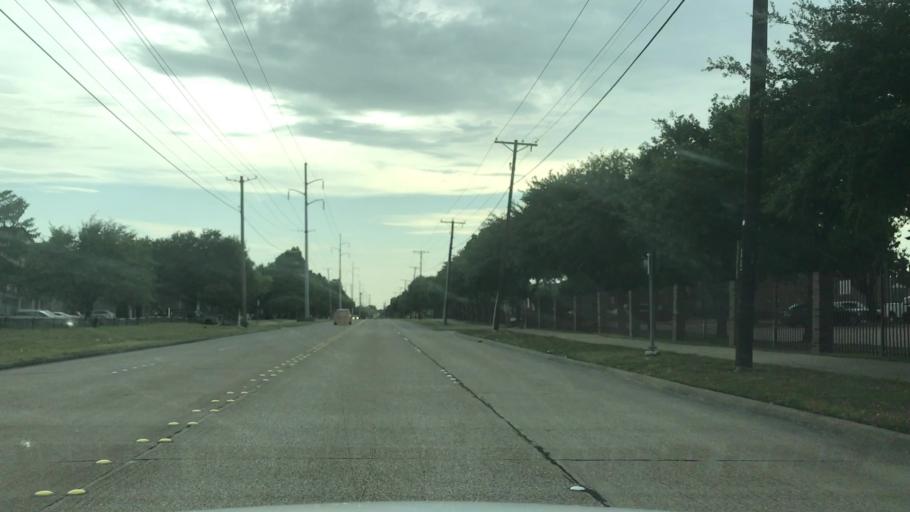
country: US
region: Texas
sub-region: Dallas County
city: Rowlett
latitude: 32.8511
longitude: -96.5730
